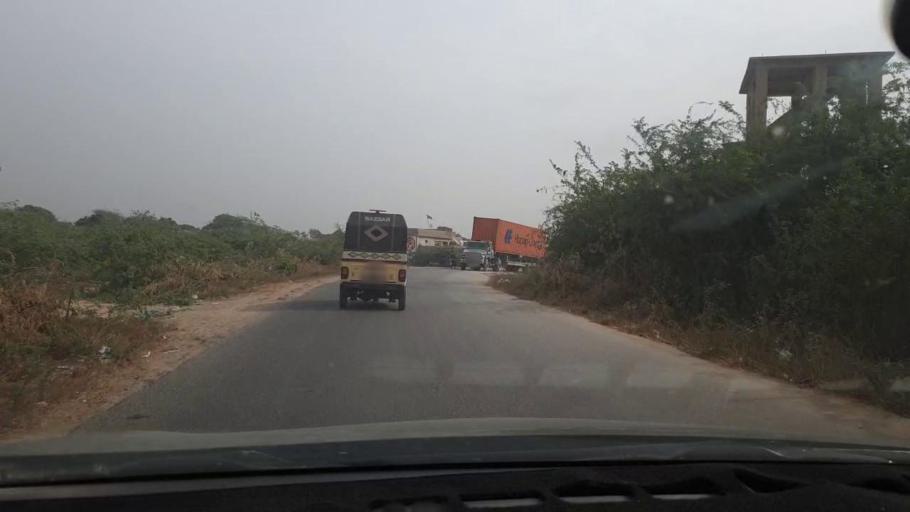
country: PK
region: Sindh
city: Malir Cantonment
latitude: 24.9100
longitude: 67.2849
